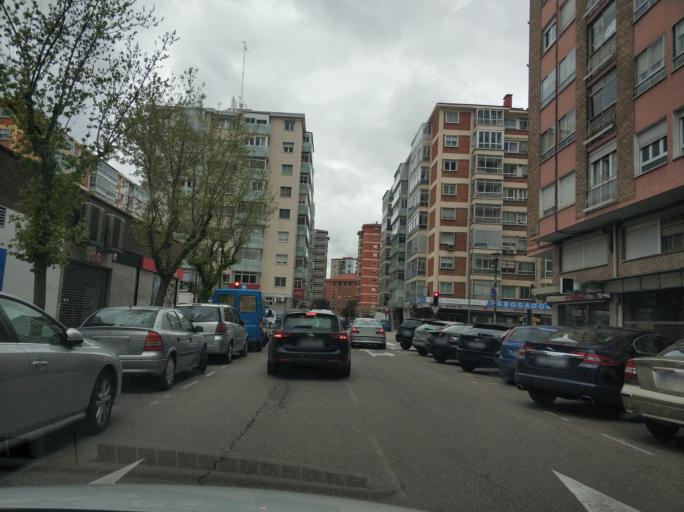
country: ES
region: Castille and Leon
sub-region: Provincia de Burgos
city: Burgos
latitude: 42.3506
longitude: -3.6730
